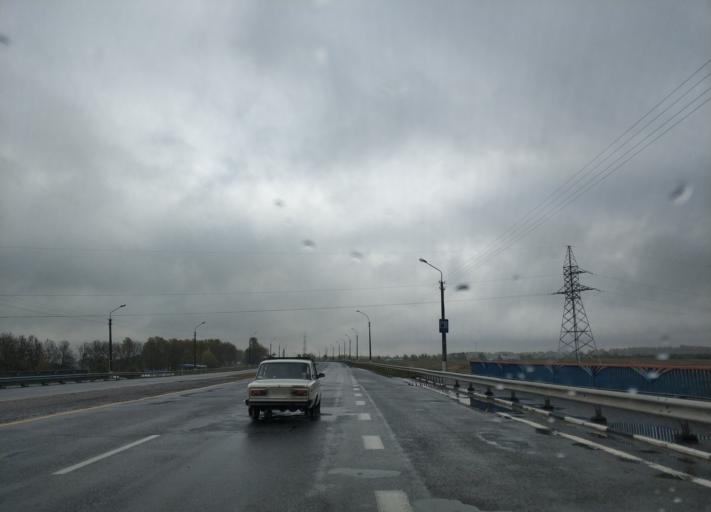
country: BY
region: Vitebsk
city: Vitebsk
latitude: 55.1926
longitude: 30.1282
